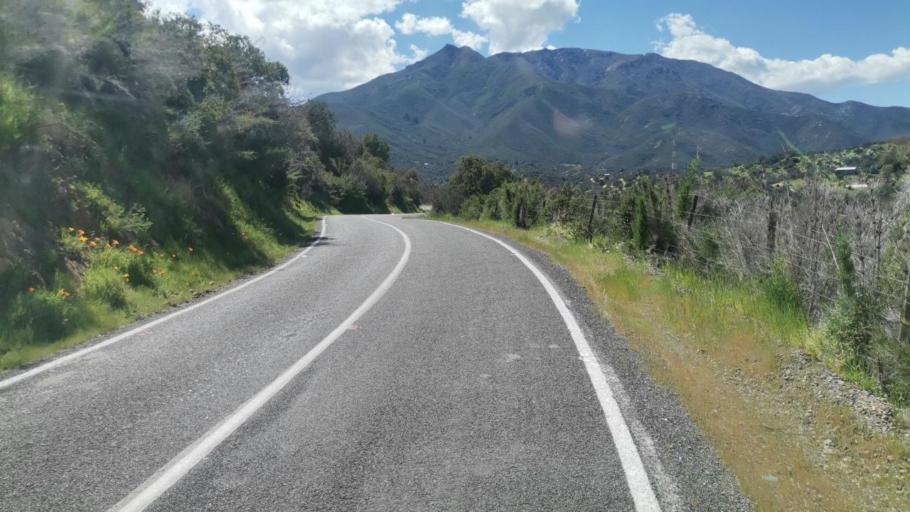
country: CL
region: Valparaiso
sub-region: Provincia de Marga Marga
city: Limache
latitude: -33.1831
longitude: -71.1737
